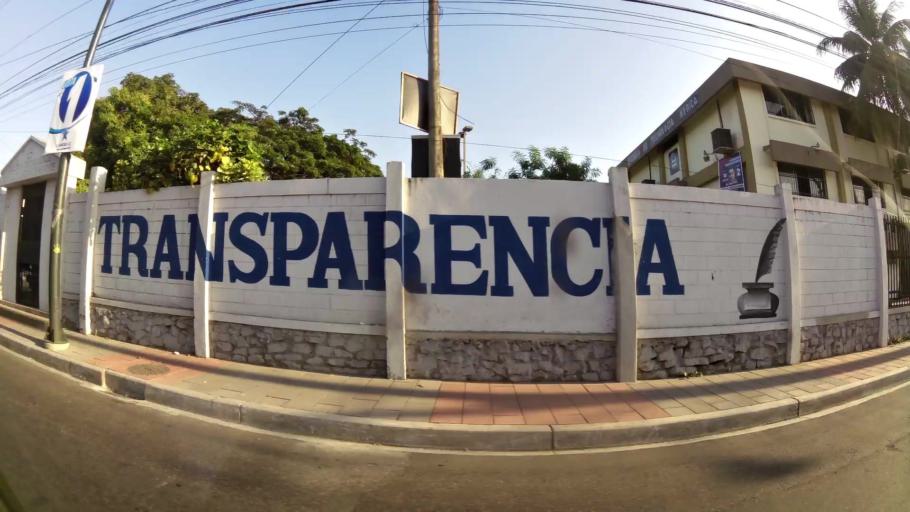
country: EC
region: Guayas
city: Guayaquil
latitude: -2.1797
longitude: -79.8983
